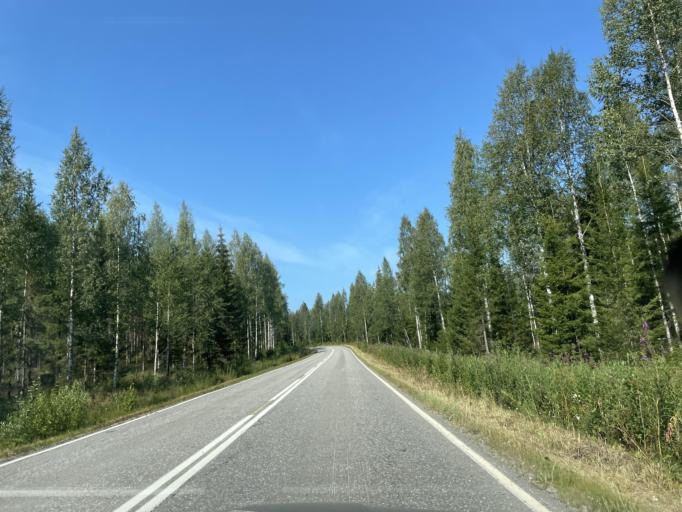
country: FI
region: Central Finland
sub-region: Saarijaervi-Viitasaari
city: Pihtipudas
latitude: 63.3667
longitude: 25.6919
